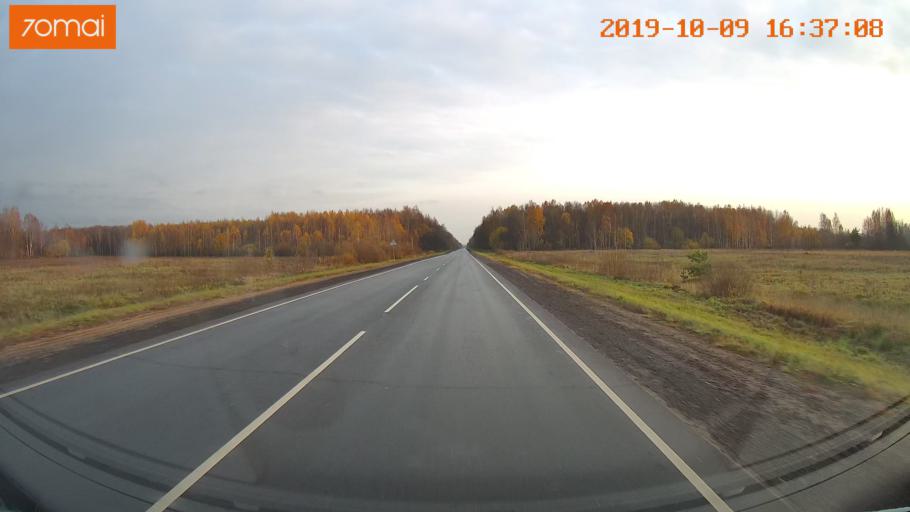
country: RU
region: Kostroma
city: Volgorechensk
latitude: 57.5315
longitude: 41.0209
